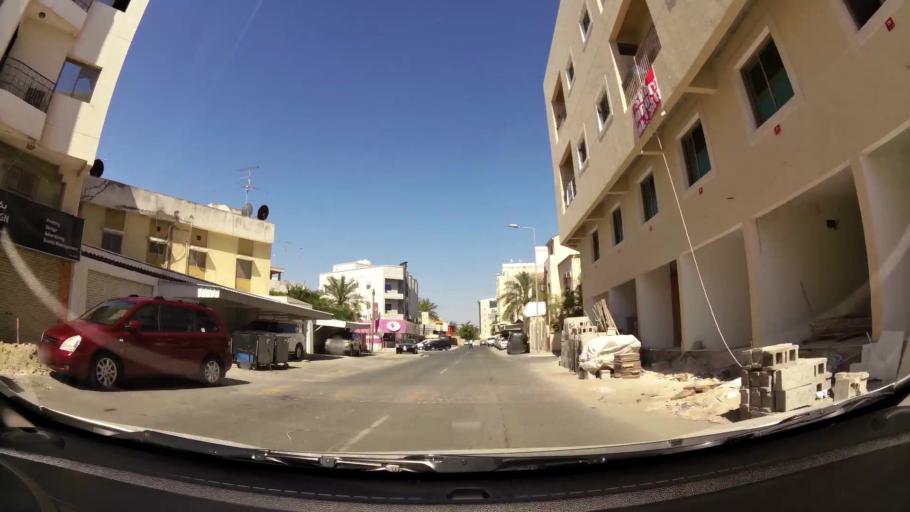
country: BH
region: Muharraq
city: Al Muharraq
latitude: 26.2622
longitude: 50.6175
